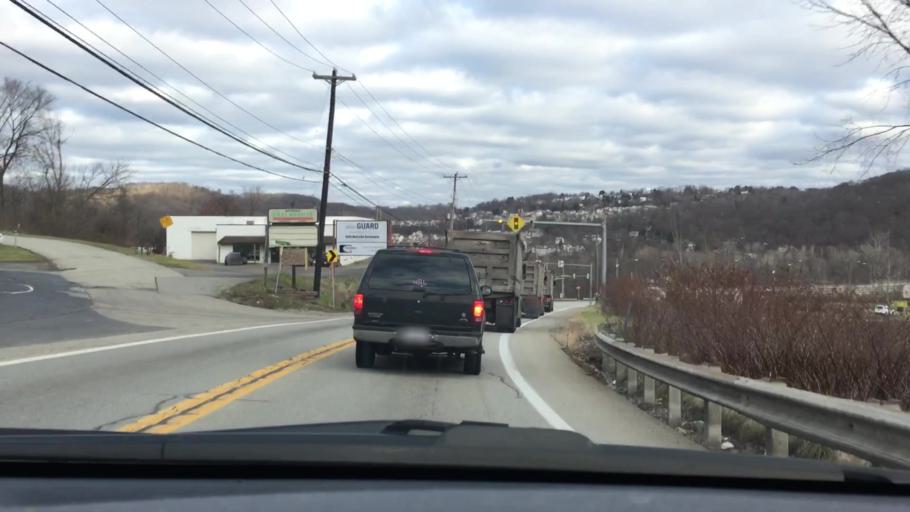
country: US
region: Pennsylvania
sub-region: Allegheny County
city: Pitcairn
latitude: 40.3916
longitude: -79.7759
